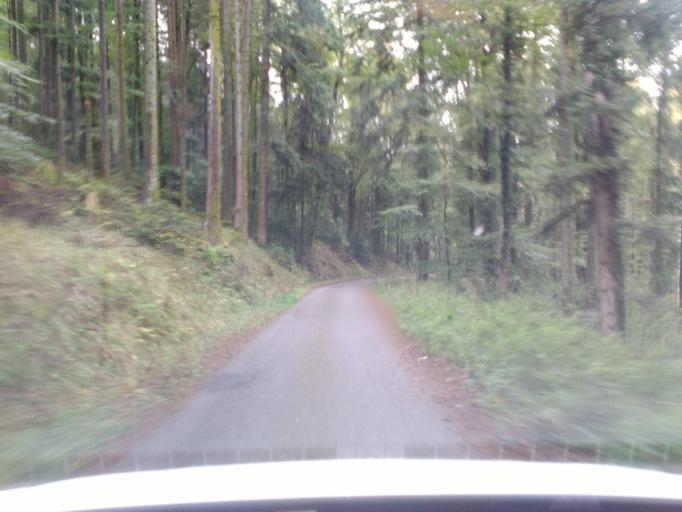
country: FR
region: Lorraine
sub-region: Departement des Vosges
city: Sainte-Marguerite
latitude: 48.3203
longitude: 7.0082
